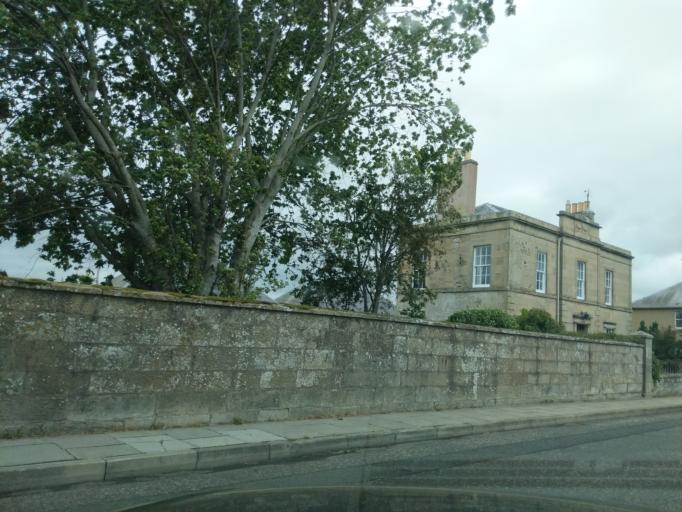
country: GB
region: Scotland
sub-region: The Scottish Borders
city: Kelso
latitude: 55.6031
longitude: -2.4422
